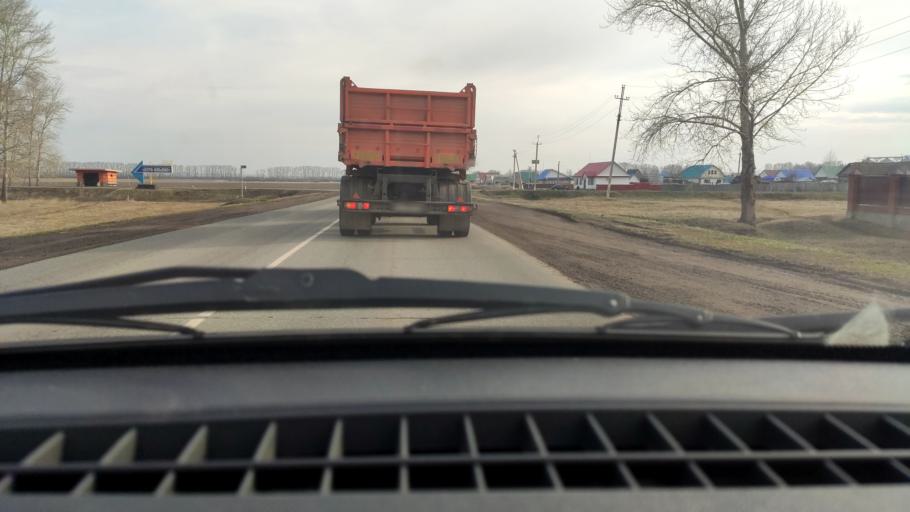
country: RU
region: Bashkortostan
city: Davlekanovo
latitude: 54.3919
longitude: 55.2041
